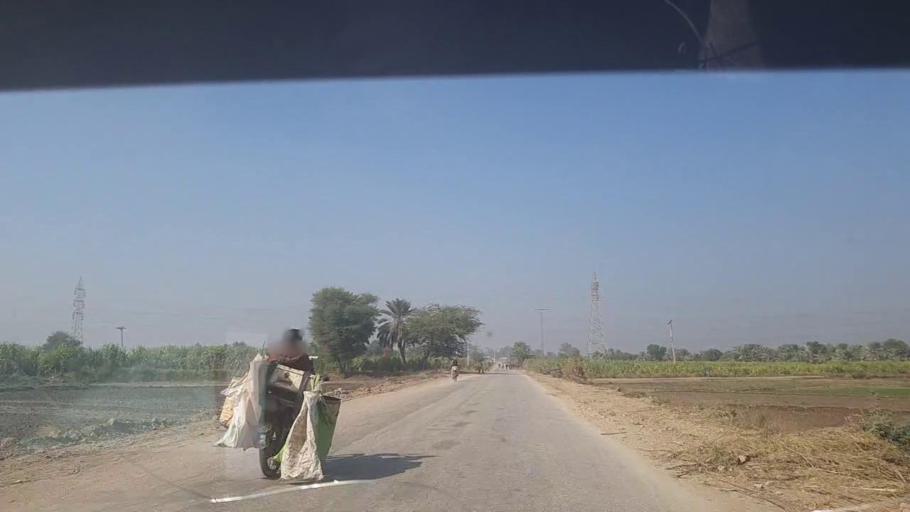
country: PK
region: Sindh
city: Kot Diji
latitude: 27.4263
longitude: 68.6562
